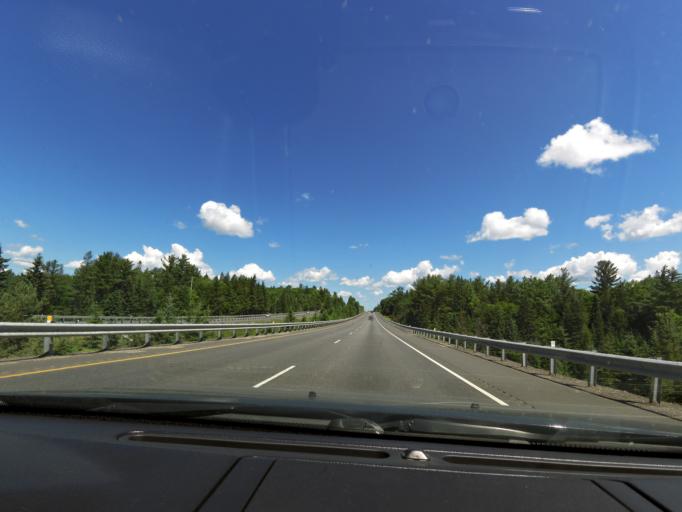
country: CA
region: Ontario
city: Bracebridge
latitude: 45.1671
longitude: -79.3115
